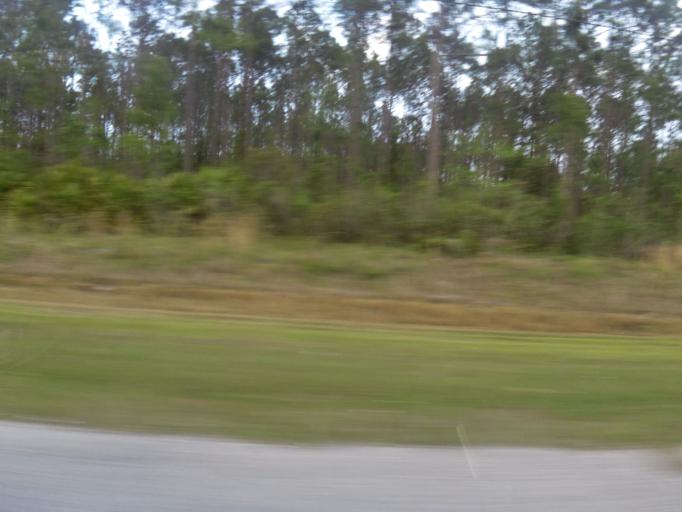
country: US
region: Florida
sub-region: Saint Johns County
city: Villano Beach
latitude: 30.0222
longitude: -81.4006
